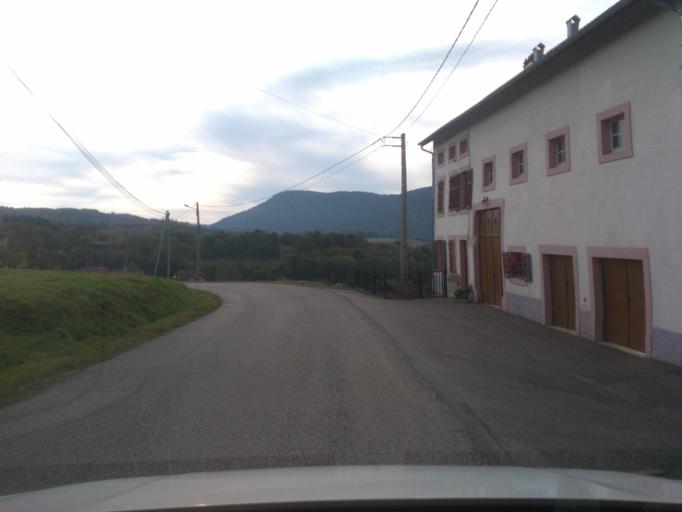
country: FR
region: Lorraine
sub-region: Departement des Vosges
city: Senones
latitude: 48.3447
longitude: 7.0084
